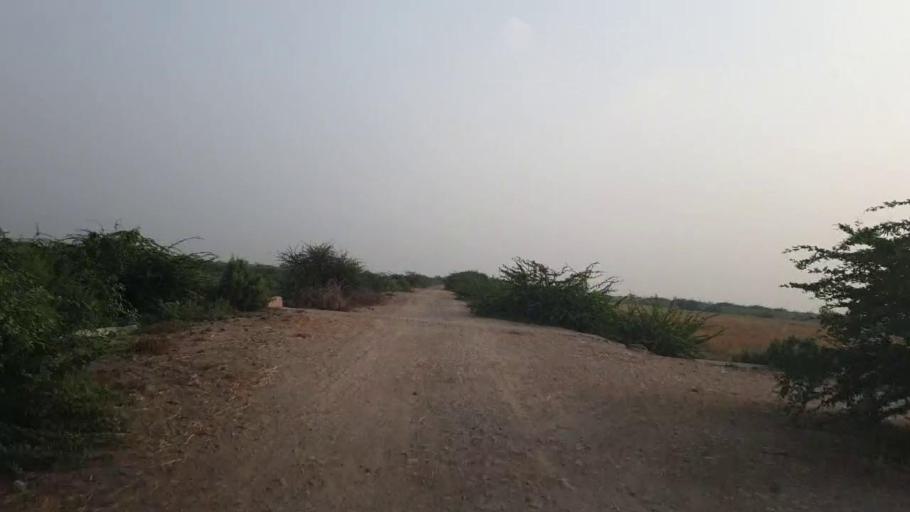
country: PK
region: Sindh
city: Mirpur Batoro
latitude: 24.6467
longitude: 68.3727
